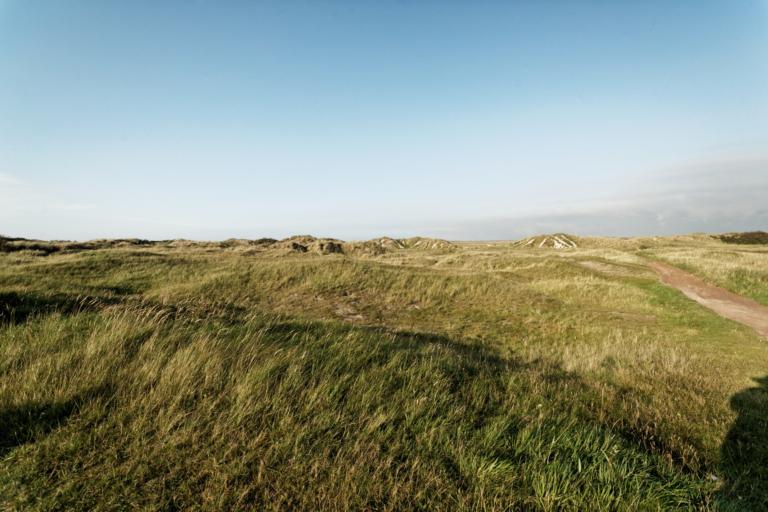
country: NL
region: North Holland
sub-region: Gemeente Texel
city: Den Burg
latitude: 53.1301
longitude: 4.8071
